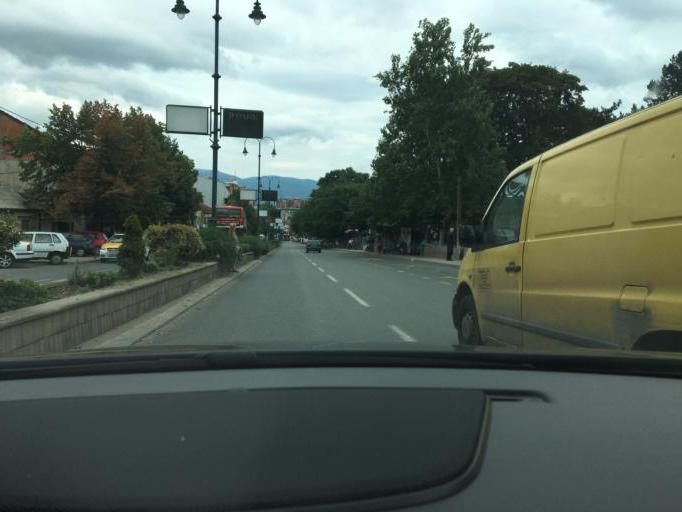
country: MK
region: Karpos
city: Skopje
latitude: 41.9887
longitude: 21.4184
